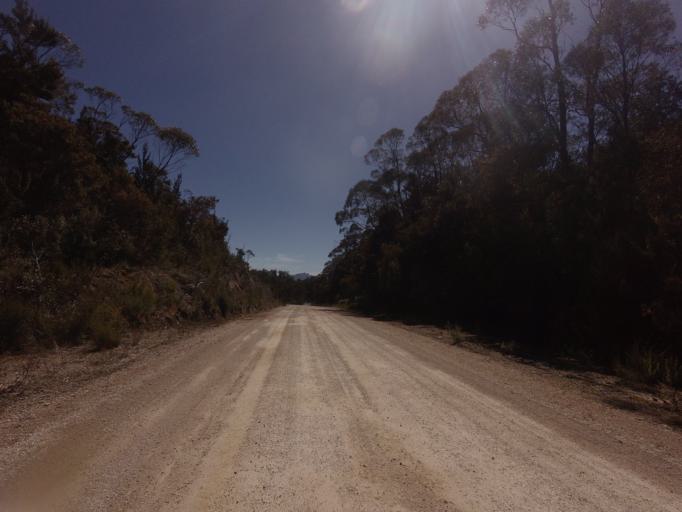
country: AU
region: Tasmania
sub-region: Huon Valley
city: Geeveston
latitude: -42.8157
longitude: 146.3859
